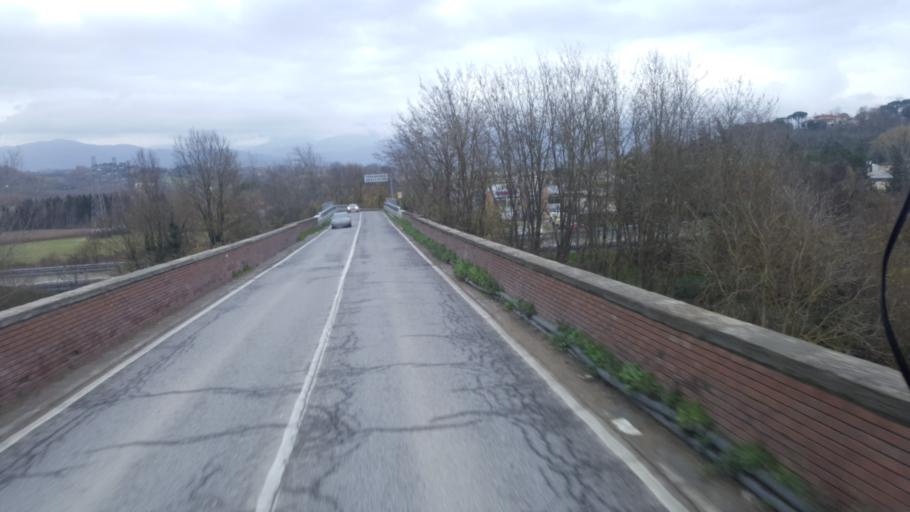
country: IT
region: Tuscany
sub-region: Province of Arezzo
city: Montevarchi
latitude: 43.5412
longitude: 11.5663
